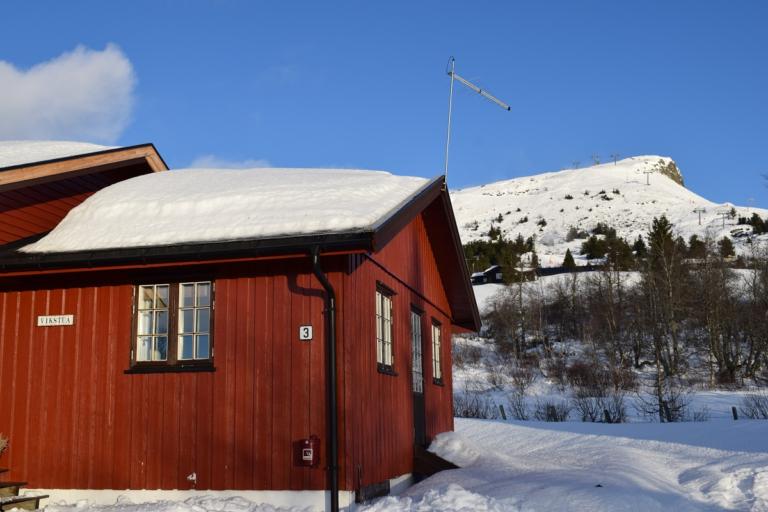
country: NO
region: Oppland
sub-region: Gausdal
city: Segalstad bru
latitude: 61.3406
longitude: 10.0821
